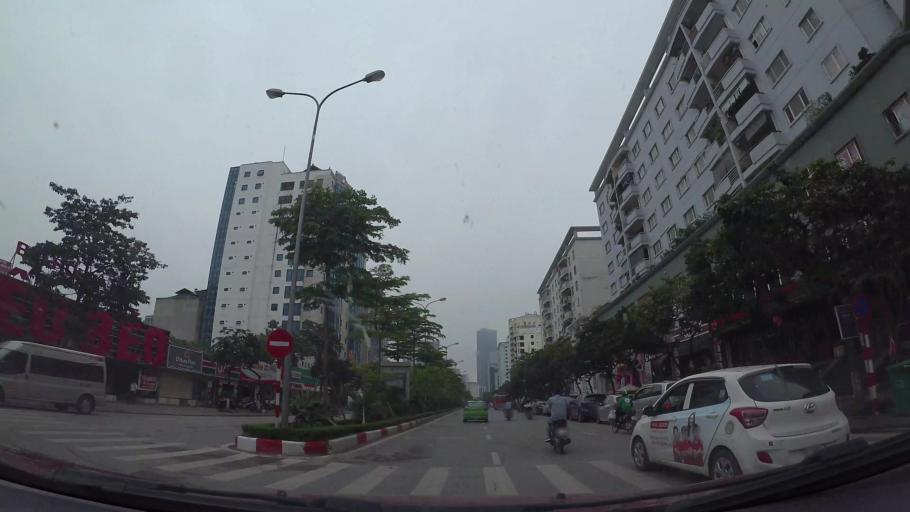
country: VN
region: Ha Noi
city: Cau Giay
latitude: 21.0331
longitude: 105.7887
